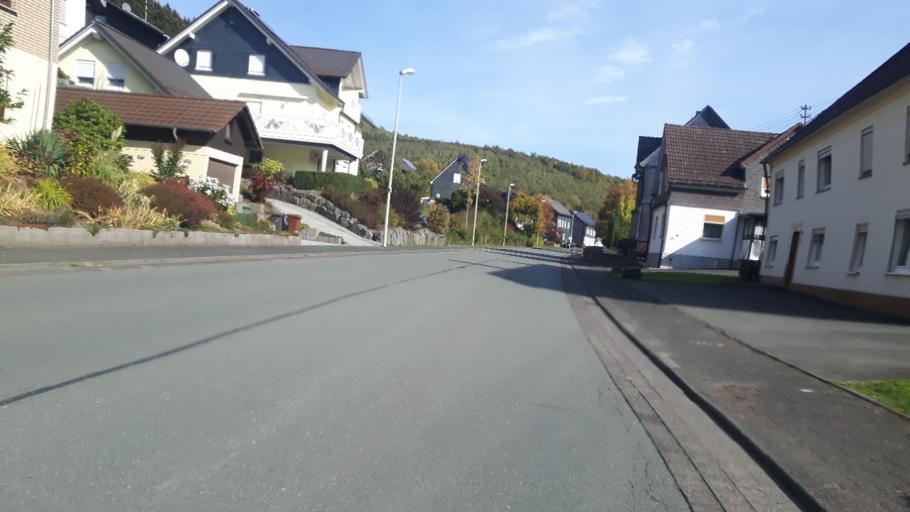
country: DE
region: North Rhine-Westphalia
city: Netphen
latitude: 50.8950
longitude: 8.1908
